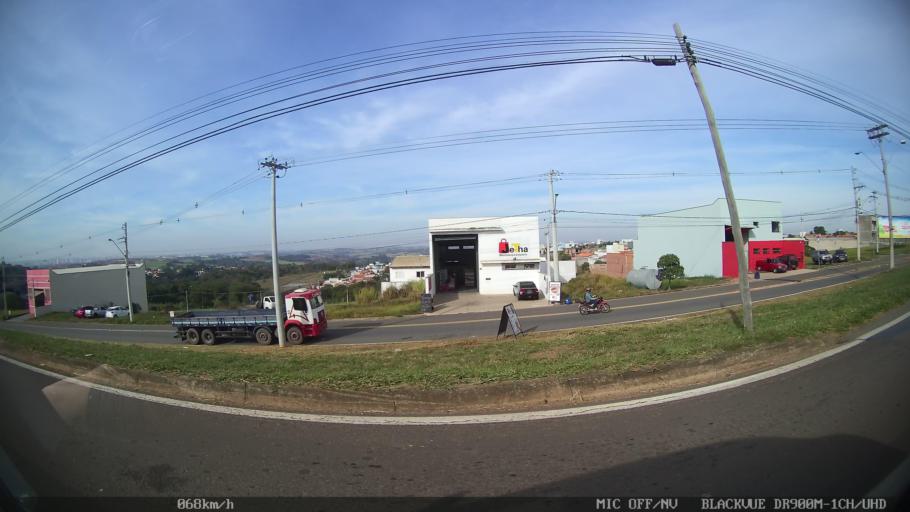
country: BR
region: Sao Paulo
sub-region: Piracicaba
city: Piracicaba
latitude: -22.6794
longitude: -47.7091
